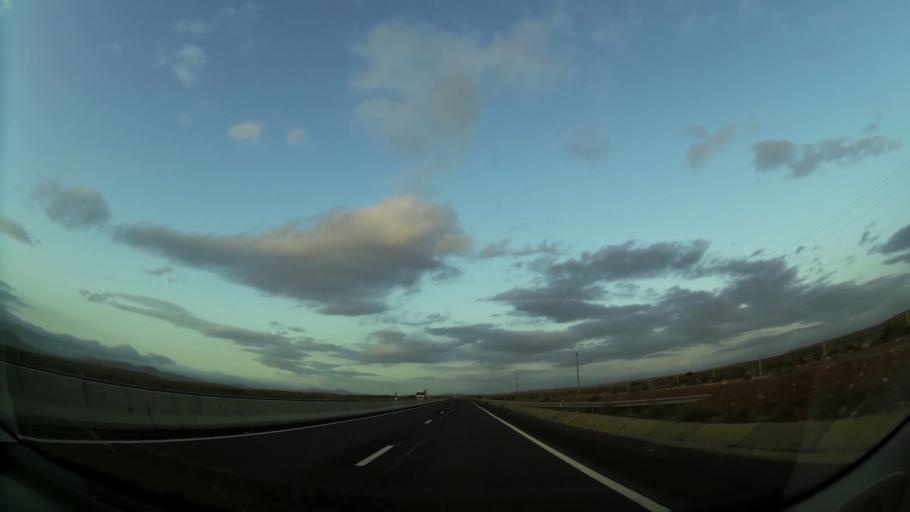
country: MA
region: Oriental
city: Taourirt
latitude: 34.5493
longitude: -2.8774
